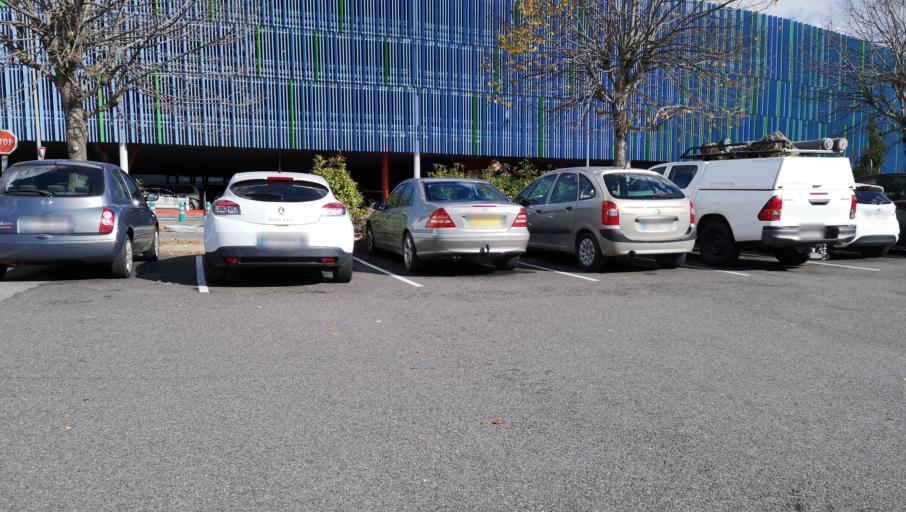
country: FR
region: Midi-Pyrenees
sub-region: Departement de la Haute-Garonne
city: Beauzelle
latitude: 43.6438
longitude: 1.3696
